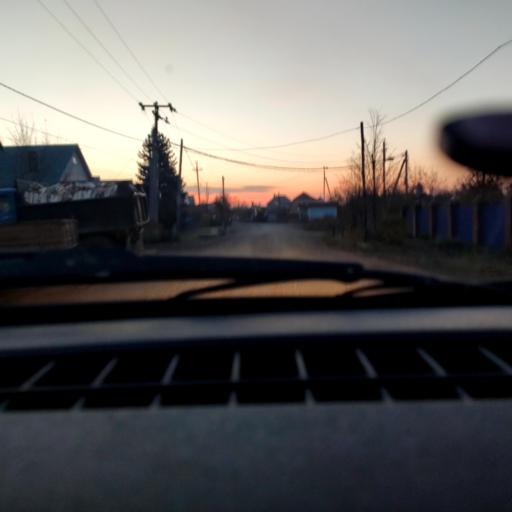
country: RU
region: Bashkortostan
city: Iglino
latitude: 54.8348
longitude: 56.1838
